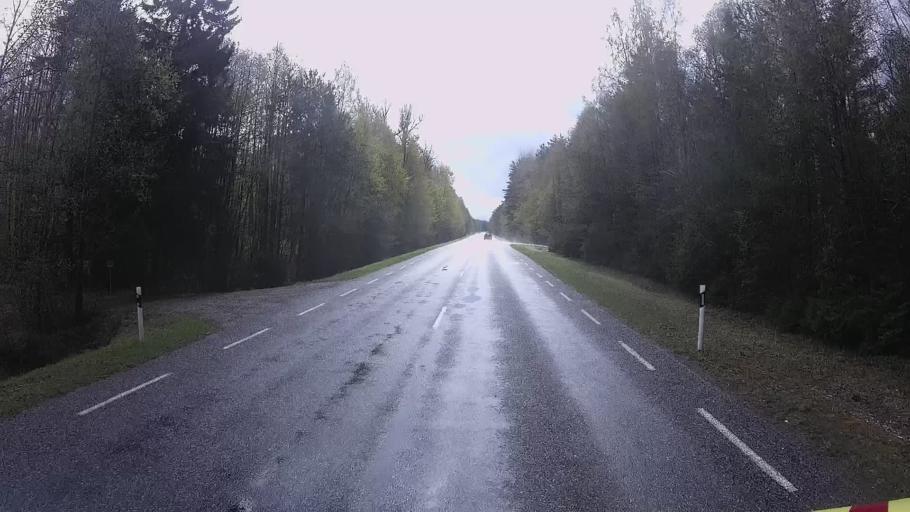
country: EE
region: Hiiumaa
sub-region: Kaerdla linn
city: Kardla
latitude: 58.9081
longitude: 22.9284
